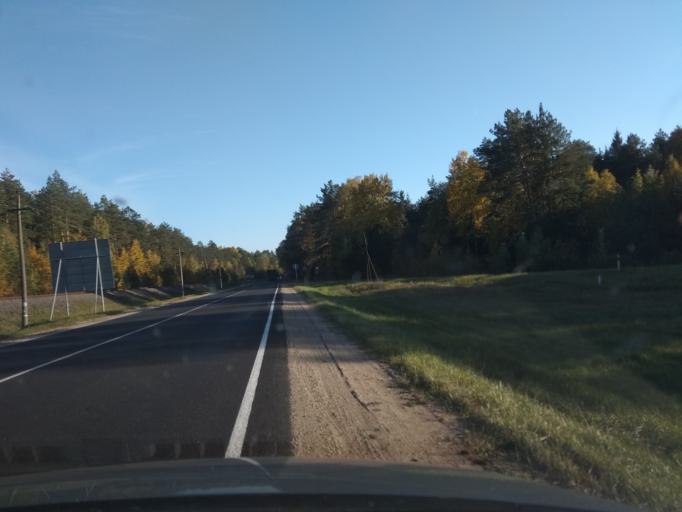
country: BY
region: Brest
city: Nyakhachava
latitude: 52.5726
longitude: 25.1155
